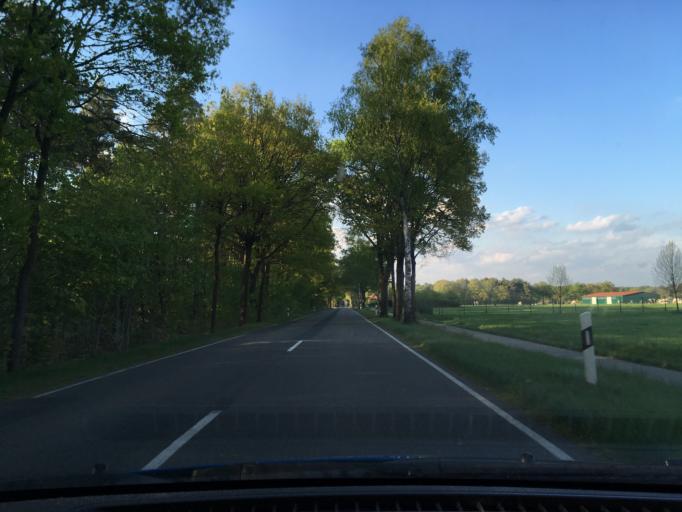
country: DE
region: Lower Saxony
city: Winsen
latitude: 52.7266
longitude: 9.9259
